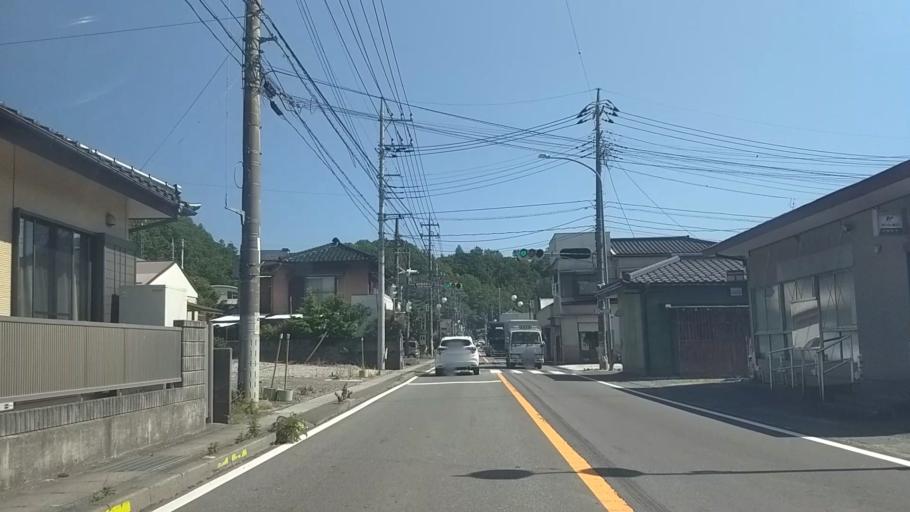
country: JP
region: Yamanashi
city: Ryuo
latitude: 35.4653
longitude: 138.4406
